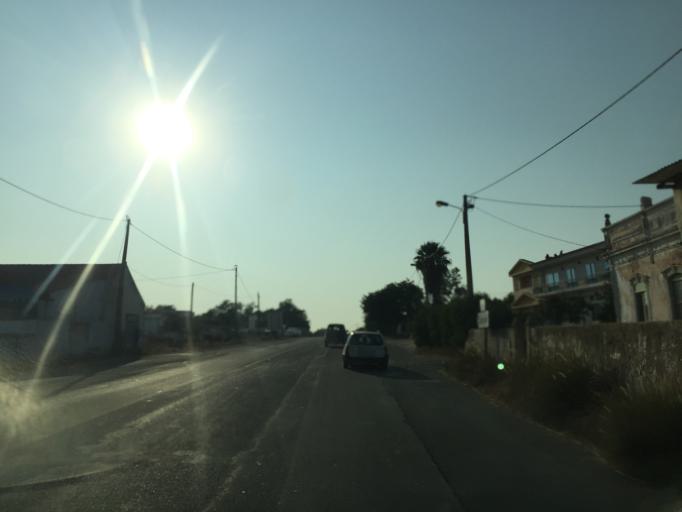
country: PT
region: Faro
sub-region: Loule
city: Almancil
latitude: 37.0805
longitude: -8.0002
